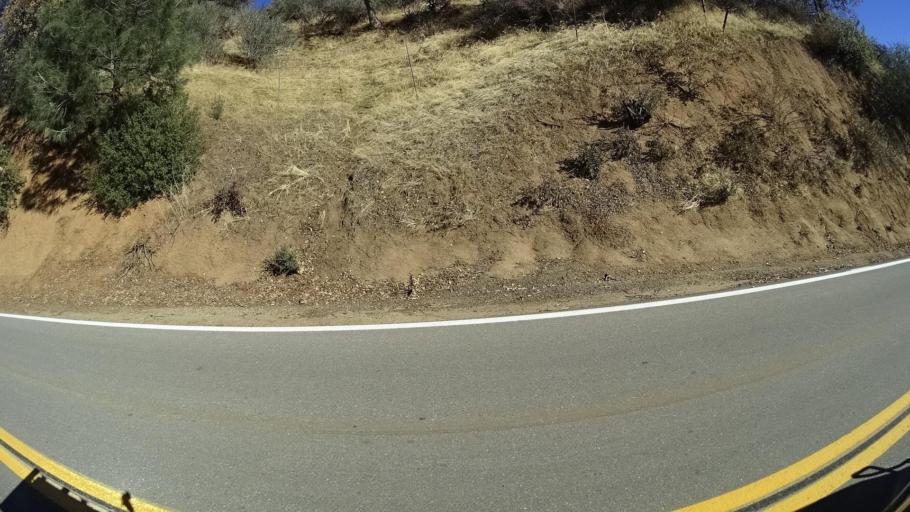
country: US
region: California
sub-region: Kern County
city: Alta Sierra
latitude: 35.7395
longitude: -118.6242
